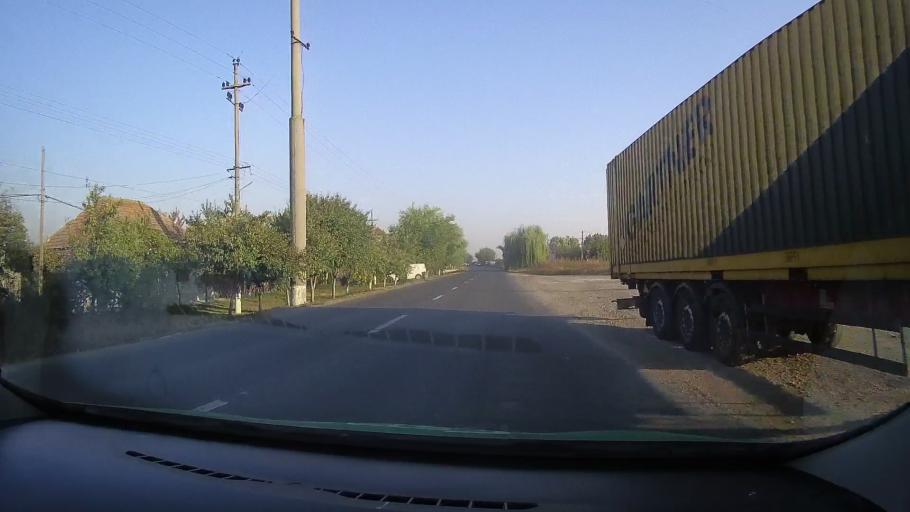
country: RO
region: Arad
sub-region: Comuna Sofronea
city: Sofronea
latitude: 46.2815
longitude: 21.3134
